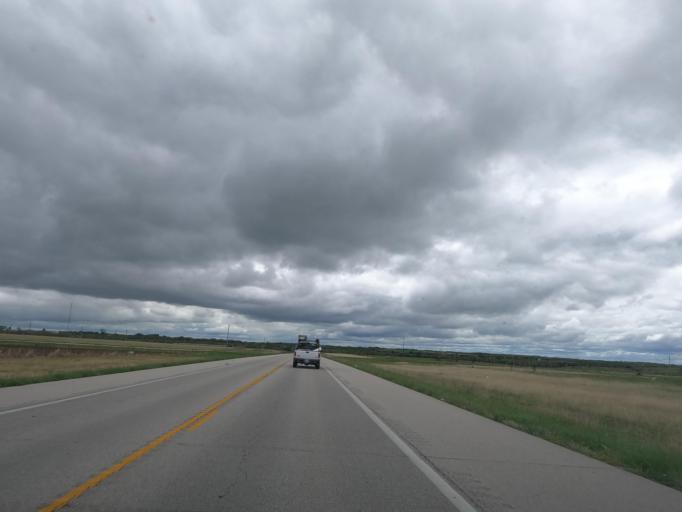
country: US
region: Kansas
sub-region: Wilson County
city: Fredonia
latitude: 37.4983
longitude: -95.7626
